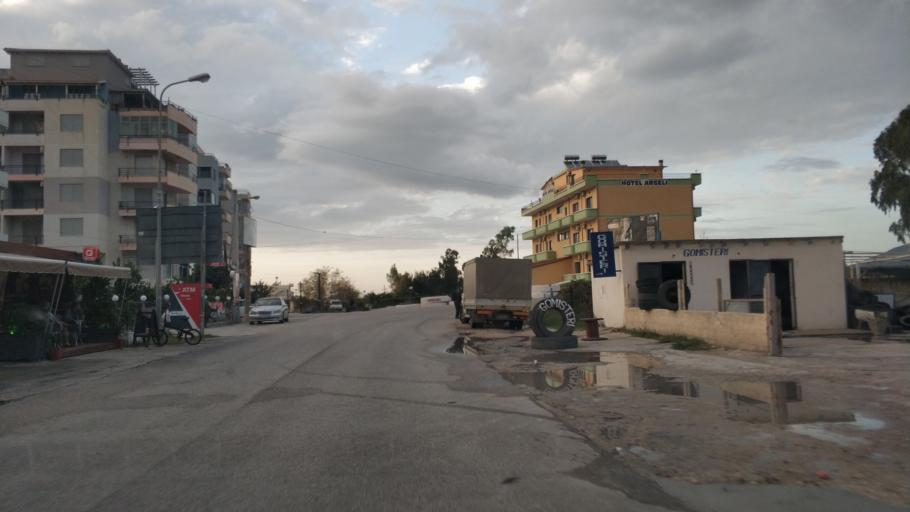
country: AL
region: Vlore
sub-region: Rrethi i Vlores
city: Orikum
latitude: 40.3309
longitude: 19.4766
